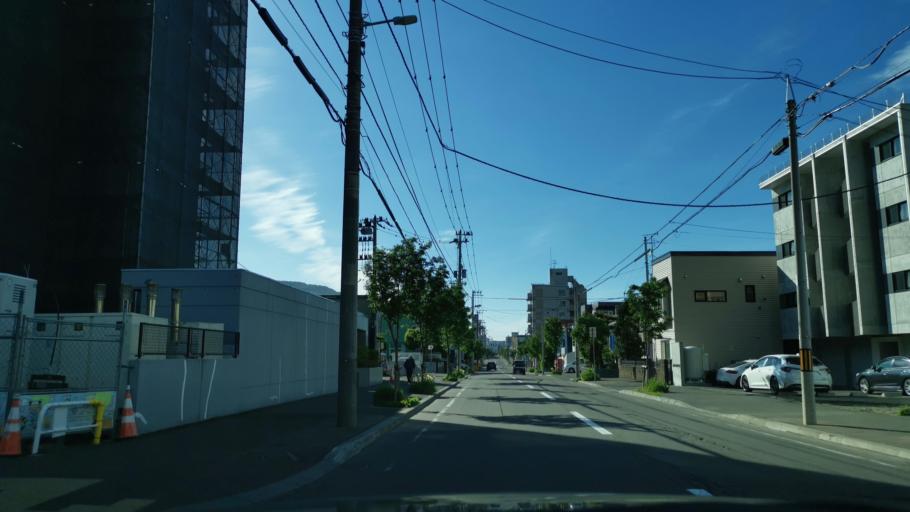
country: JP
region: Hokkaido
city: Sapporo
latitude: 43.0778
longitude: 141.2850
